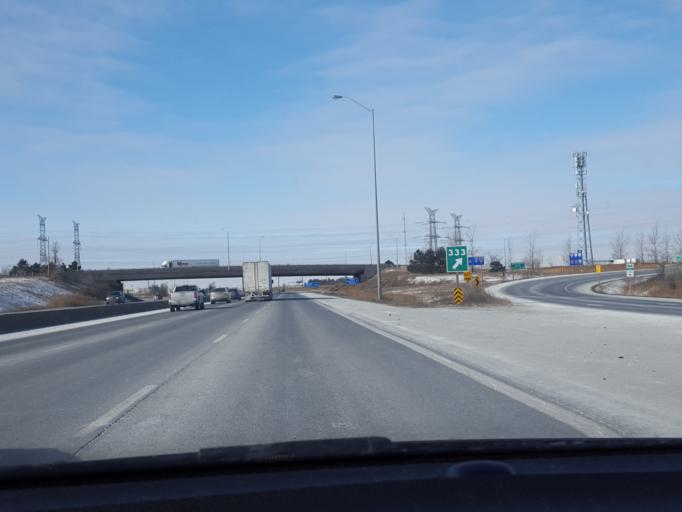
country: CA
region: Ontario
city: Brampton
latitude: 43.6007
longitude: -79.7846
